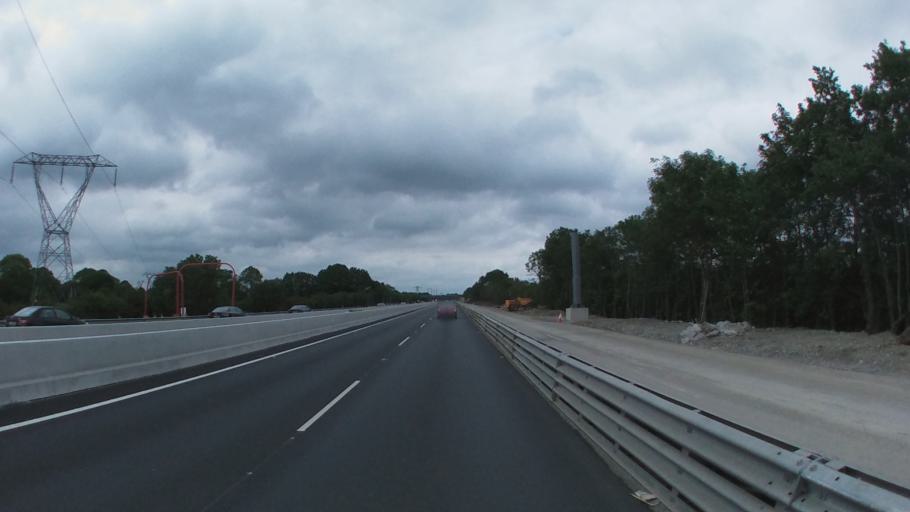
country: IE
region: Leinster
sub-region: Kildare
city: Naas
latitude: 53.2289
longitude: -6.6917
